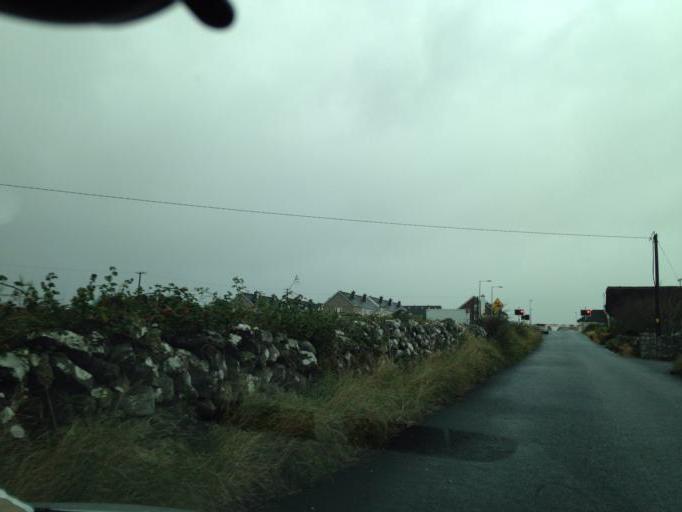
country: IE
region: Connaught
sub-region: County Galway
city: Oranmore
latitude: 53.2720
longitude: -8.9732
